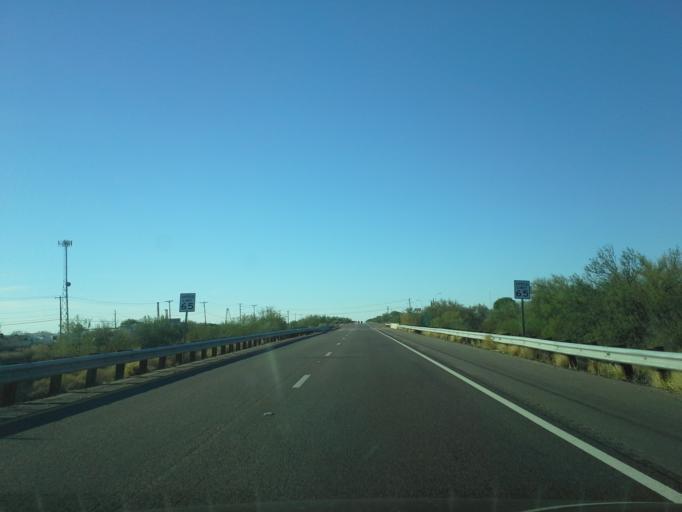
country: US
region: Arizona
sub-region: Pinal County
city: Gold Camp
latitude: 33.2970
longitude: -111.3919
